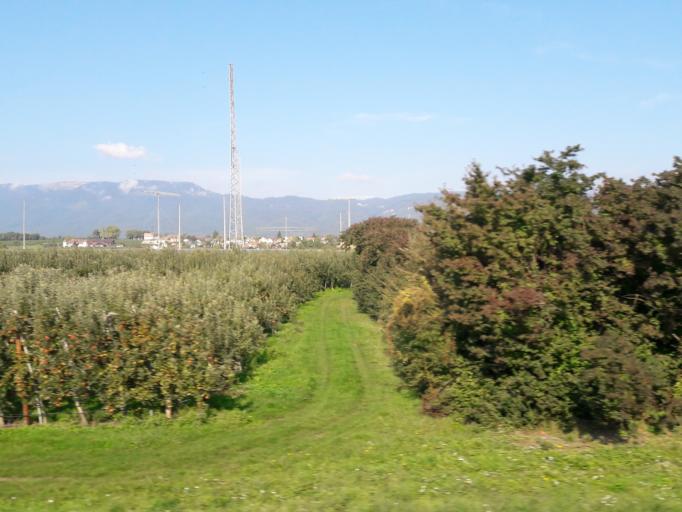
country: CH
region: Vaud
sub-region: Nyon District
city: Prangins
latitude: 46.4040
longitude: 6.2540
